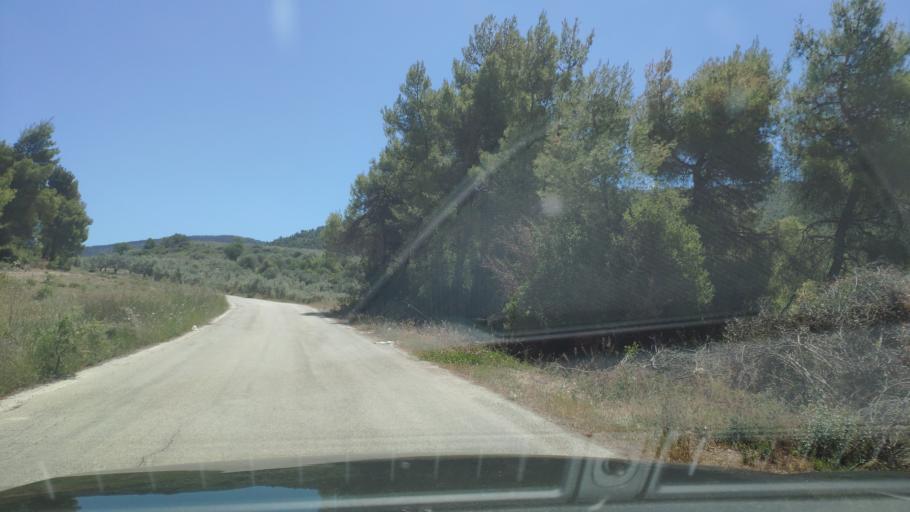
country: GR
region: Peloponnese
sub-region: Nomos Korinthias
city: Khiliomodhi
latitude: 37.8021
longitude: 22.8976
